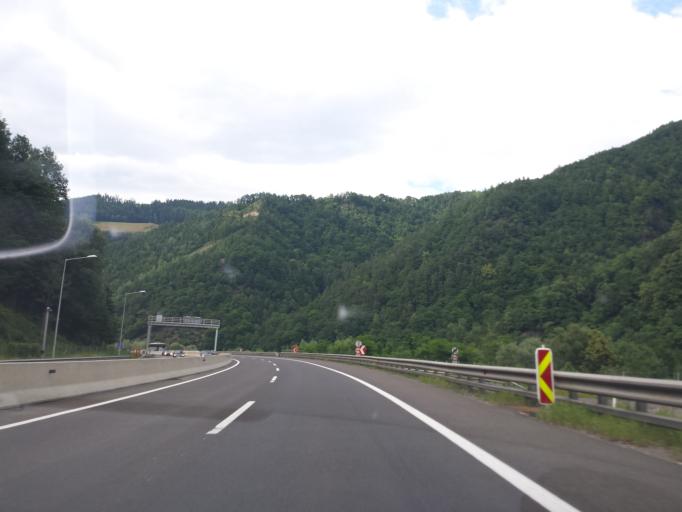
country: AT
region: Styria
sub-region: Politischer Bezirk Bruck-Muerzzuschlag
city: Bruck an der Mur
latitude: 47.3890
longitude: 15.3100
